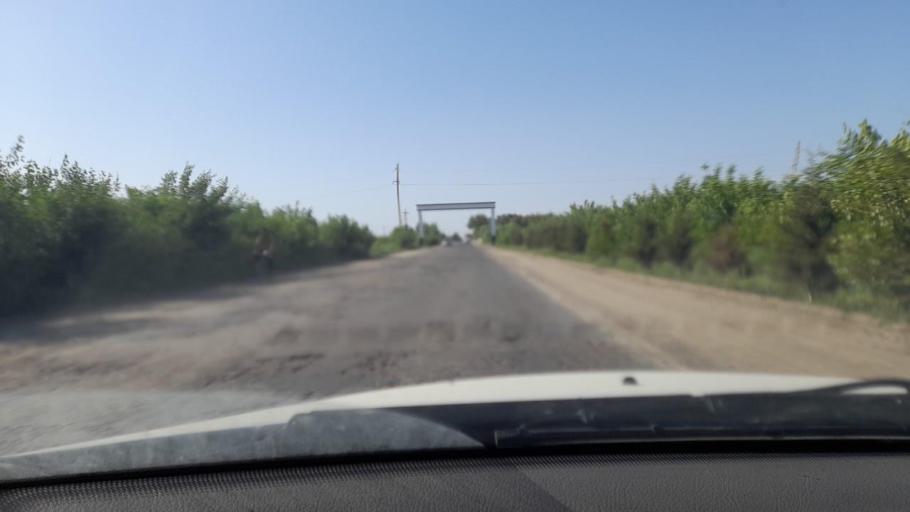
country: UZ
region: Bukhara
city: Romiton
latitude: 40.0666
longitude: 64.3270
